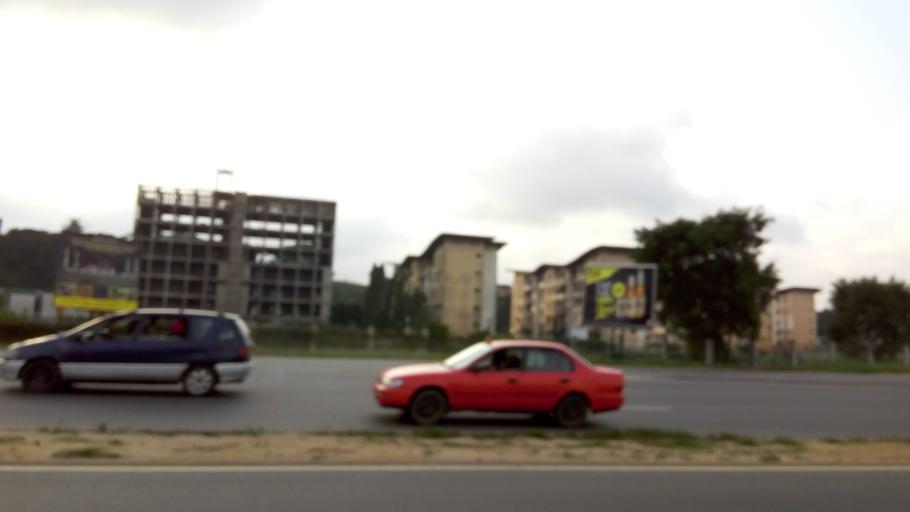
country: CI
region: Lagunes
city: Abidjan
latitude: 5.3445
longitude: -4.0167
